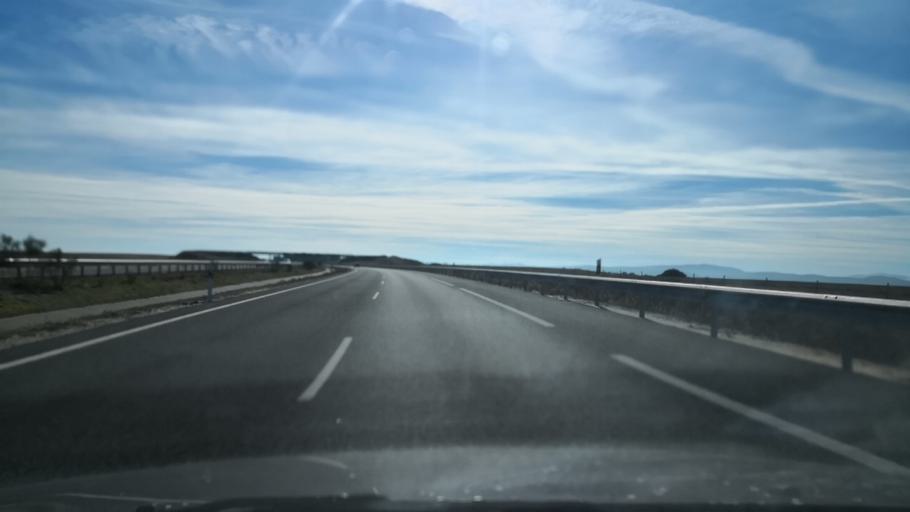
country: ES
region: Castille and Leon
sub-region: Provincia de Avila
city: Crespos
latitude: 40.8581
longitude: -4.9842
